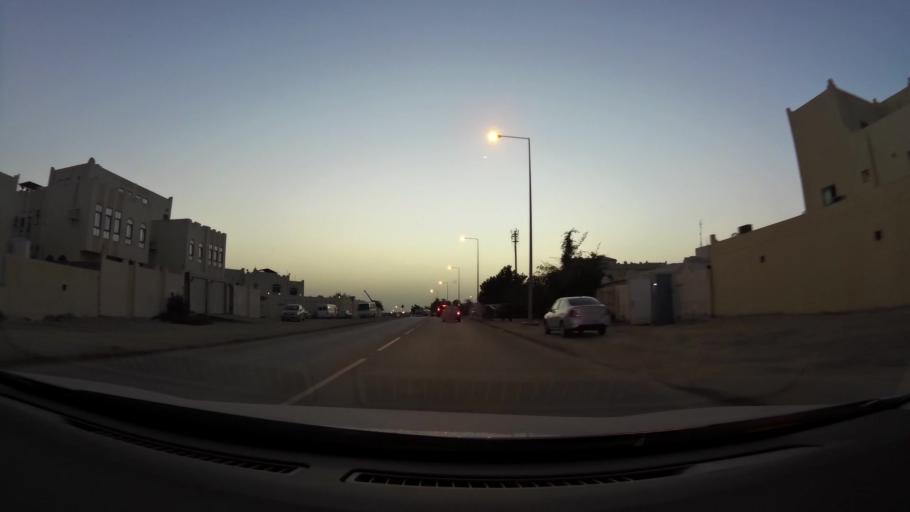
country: QA
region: Baladiyat ar Rayyan
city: Ar Rayyan
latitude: 25.3135
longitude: 51.4555
